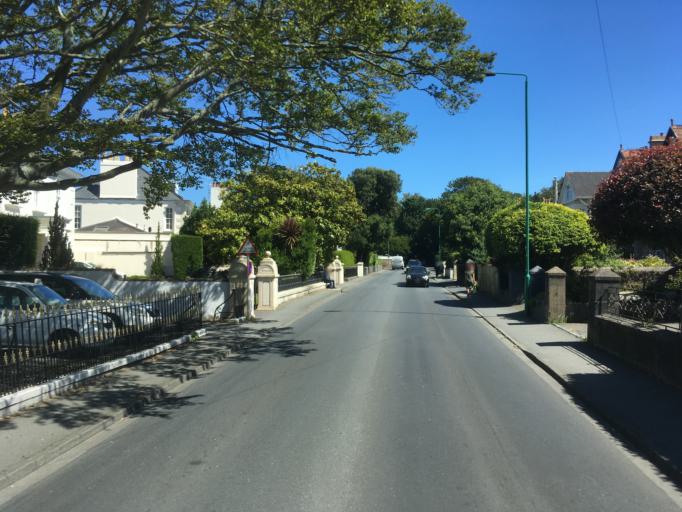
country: GG
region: St Peter Port
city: Saint Peter Port
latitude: 49.4593
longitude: -2.5547
